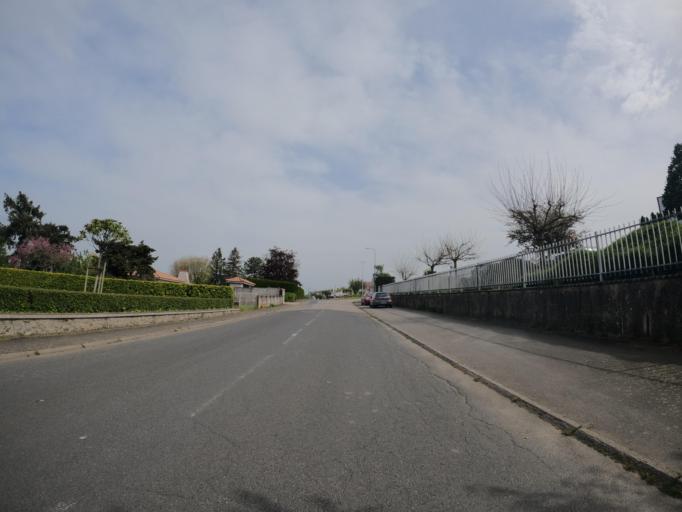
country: FR
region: Poitou-Charentes
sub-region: Departement des Deux-Sevres
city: La Chapelle-Saint-Laurent
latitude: 46.6948
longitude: -0.4995
